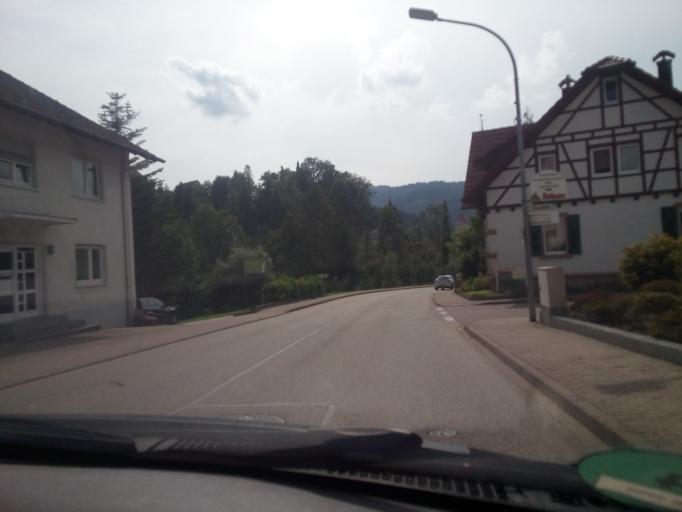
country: DE
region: Baden-Wuerttemberg
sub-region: Freiburg Region
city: Ottenhofen im Schwarzwald
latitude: 48.5678
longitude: 8.1592
